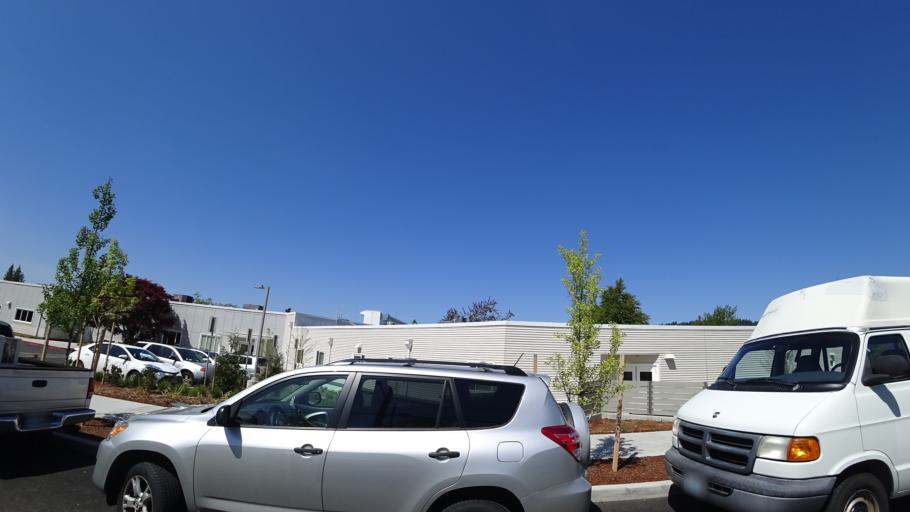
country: US
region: Oregon
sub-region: Washington County
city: Raleigh Hills
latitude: 45.4858
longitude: -122.7393
